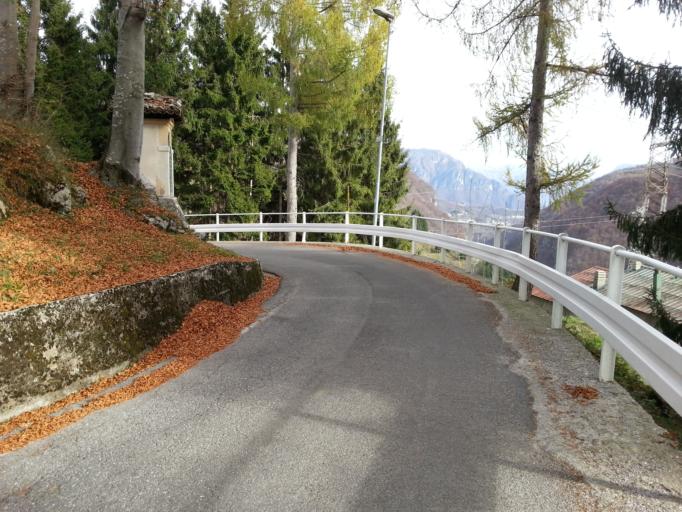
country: IT
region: Lombardy
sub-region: Provincia di Lecco
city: Morterone
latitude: 45.8820
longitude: 9.4852
